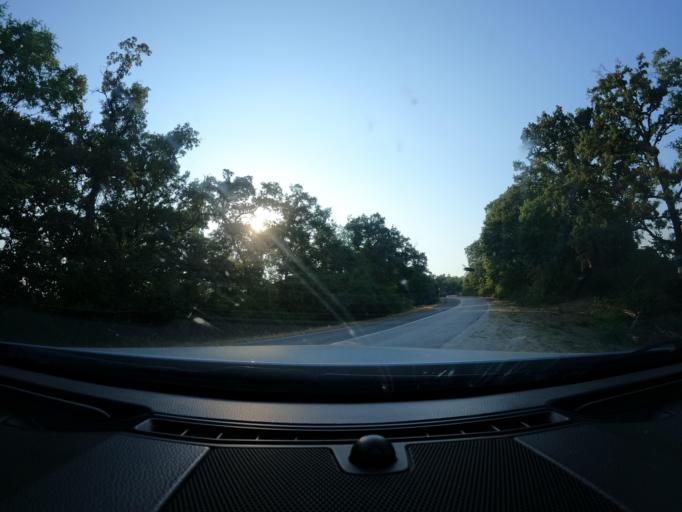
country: RS
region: Autonomna Pokrajina Vojvodina
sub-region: Juznobacki Okrug
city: Beocin
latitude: 45.1670
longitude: 19.7129
